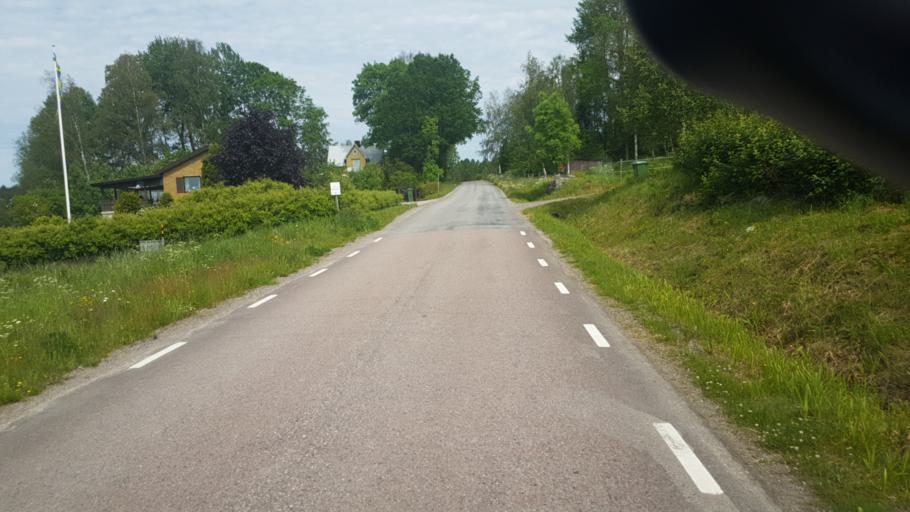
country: SE
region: Vaermland
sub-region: Eda Kommun
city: Amotfors
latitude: 59.7609
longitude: 12.4438
